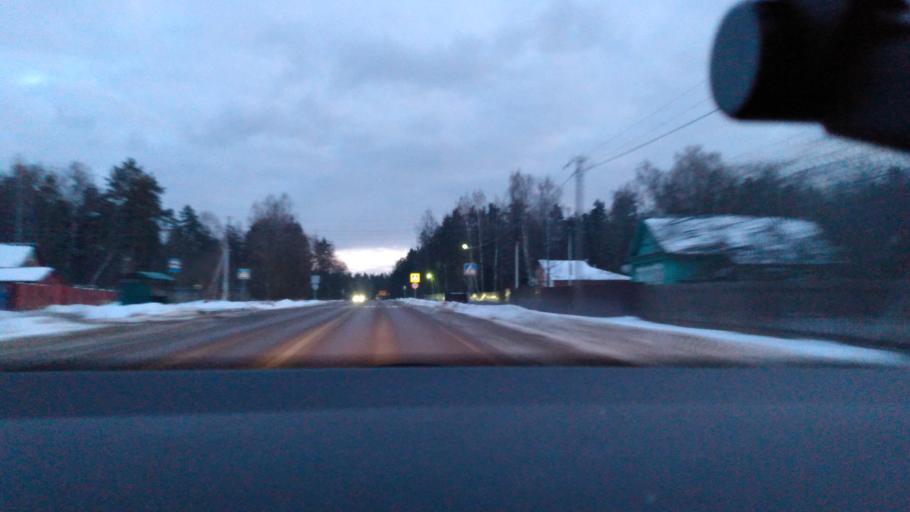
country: RU
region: Moskovskaya
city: Yegor'yevsk
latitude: 55.2873
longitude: 39.0864
